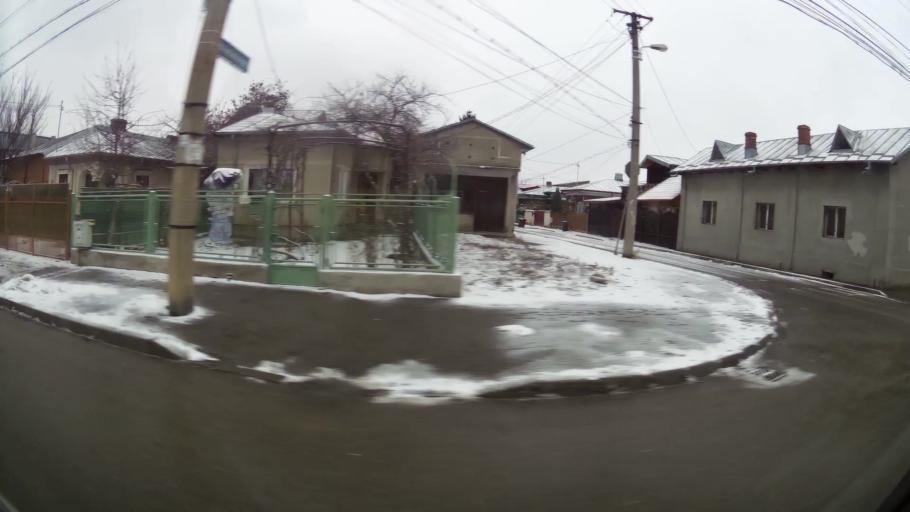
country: RO
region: Prahova
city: Ploiesti
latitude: 44.9305
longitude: 26.0436
